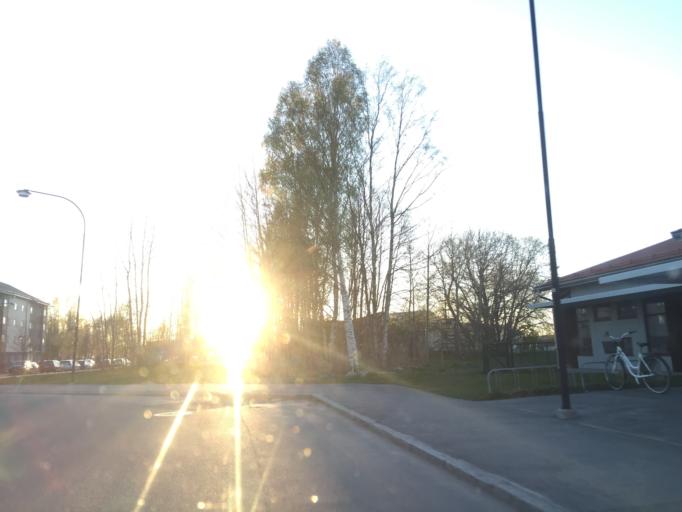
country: SE
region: OErebro
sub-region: Orebro Kommun
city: Orebro
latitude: 59.2579
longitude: 15.2143
